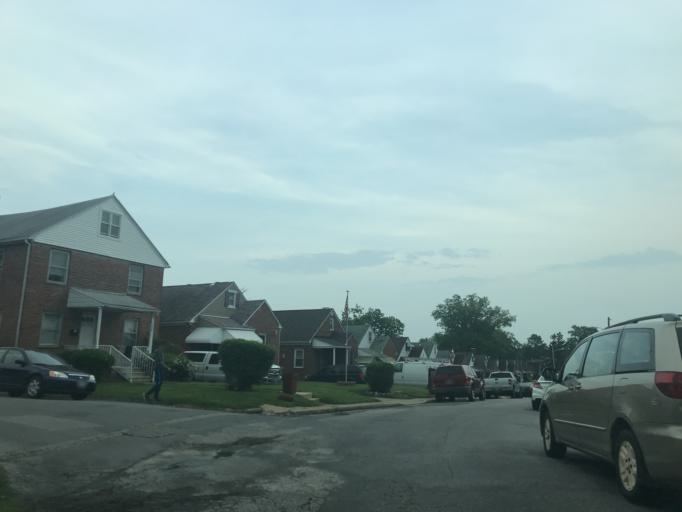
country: US
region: Maryland
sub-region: Baltimore County
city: Parkville
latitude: 39.3817
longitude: -76.5423
